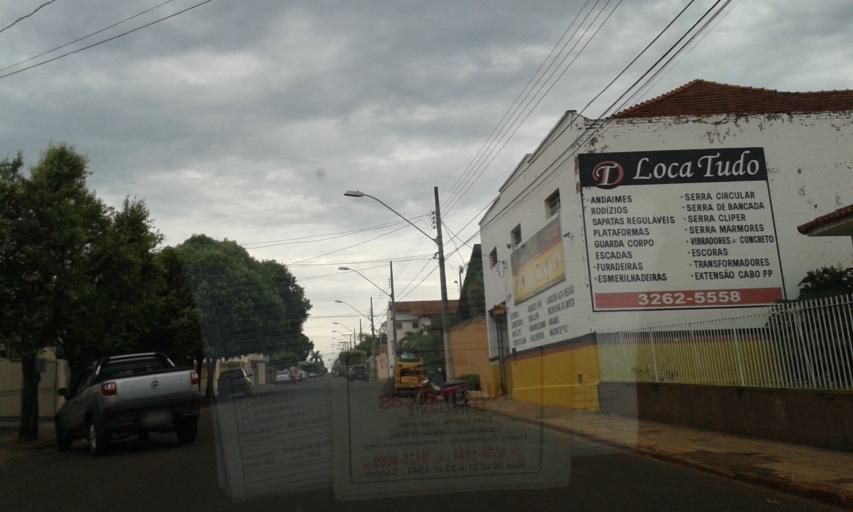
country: BR
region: Minas Gerais
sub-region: Ituiutaba
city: Ituiutaba
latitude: -18.9798
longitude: -49.4599
